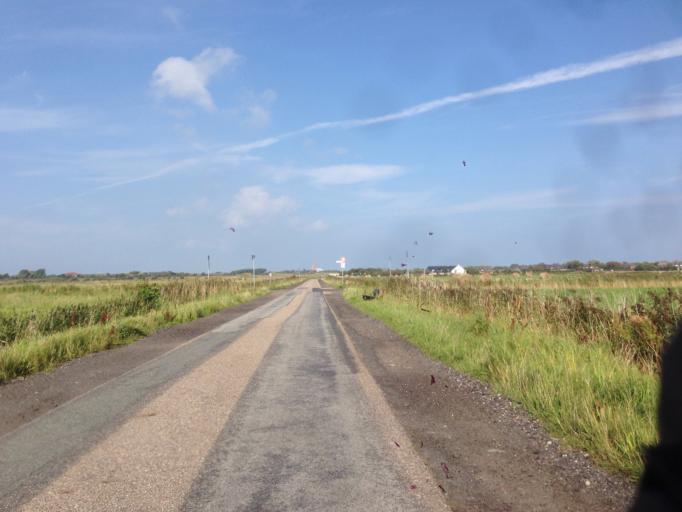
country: DE
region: Schleswig-Holstein
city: Tinnum
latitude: 54.8864
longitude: 8.3510
